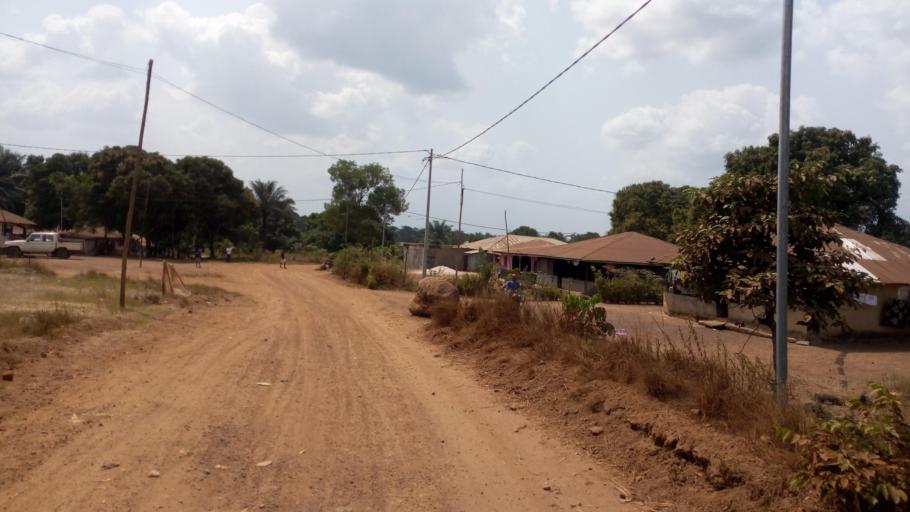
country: SL
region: Southern Province
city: Mogbwemo
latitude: 7.7942
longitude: -12.2993
